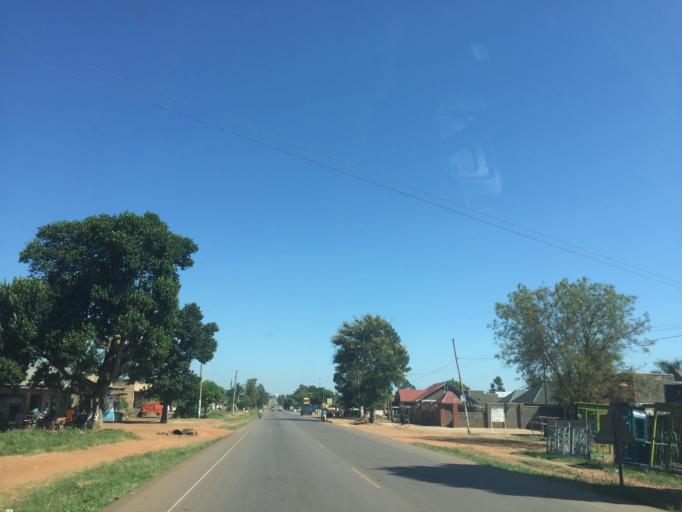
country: UG
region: Central Region
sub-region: Luwero District
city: Luwero
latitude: 0.8148
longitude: 32.5043
